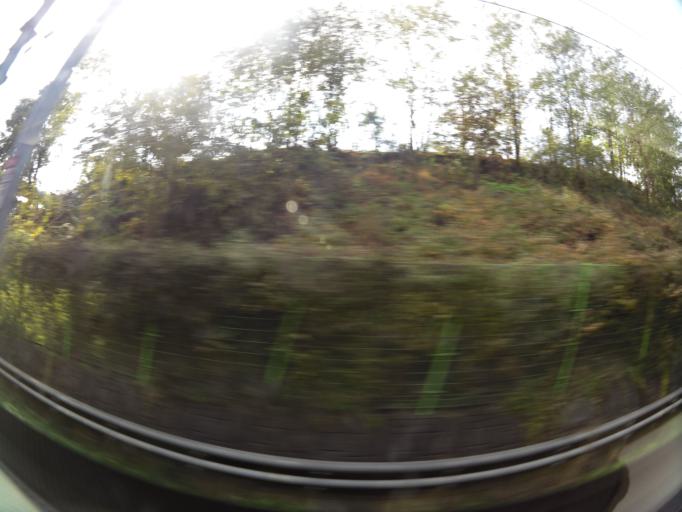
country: KR
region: Daejeon
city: Songgang-dong
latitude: 36.5431
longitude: 127.3351
